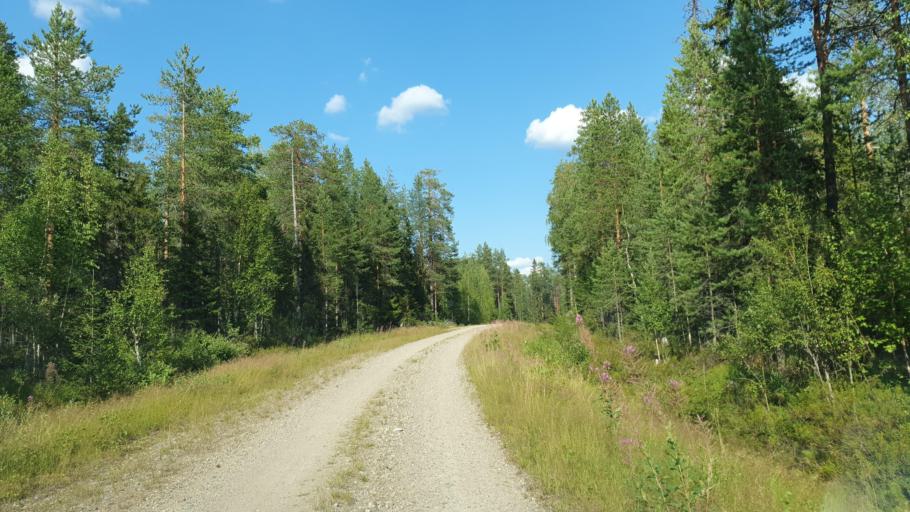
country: FI
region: Kainuu
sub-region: Kehys-Kainuu
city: Kuhmo
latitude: 63.9638
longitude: 29.5404
